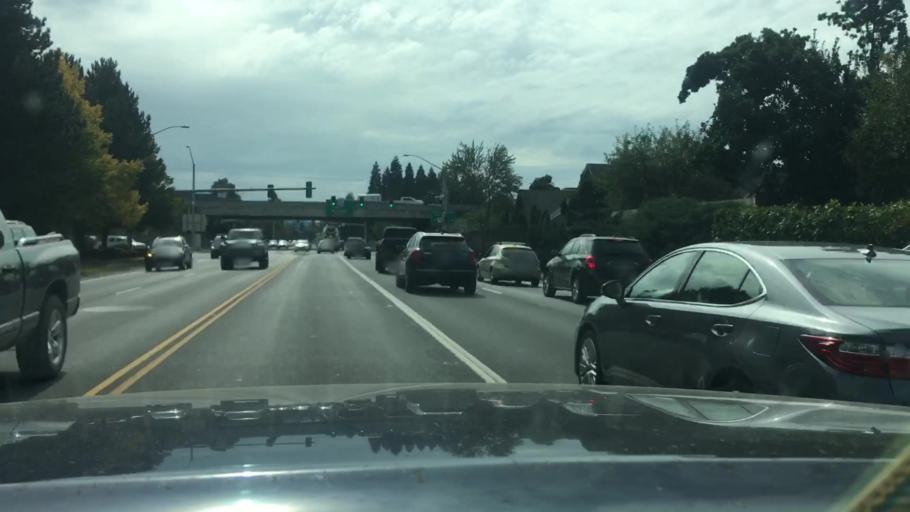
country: US
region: Oregon
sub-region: Lane County
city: Eugene
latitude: 44.0890
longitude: -123.0677
